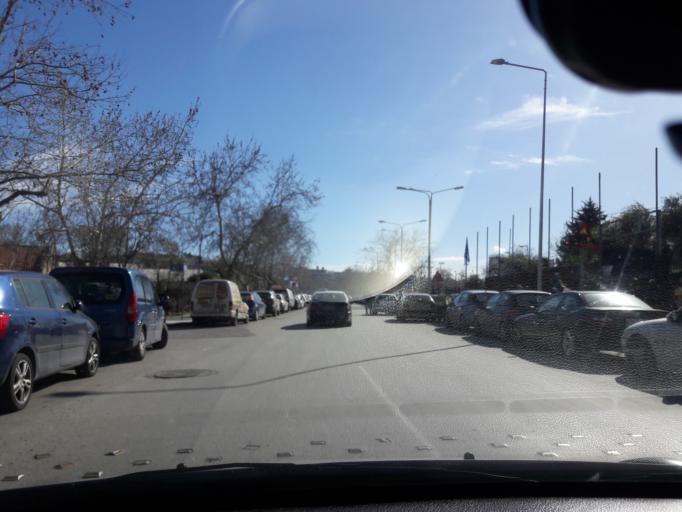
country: GR
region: Central Macedonia
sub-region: Nomos Thessalonikis
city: Kalamaria
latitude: 40.5979
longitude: 22.9508
